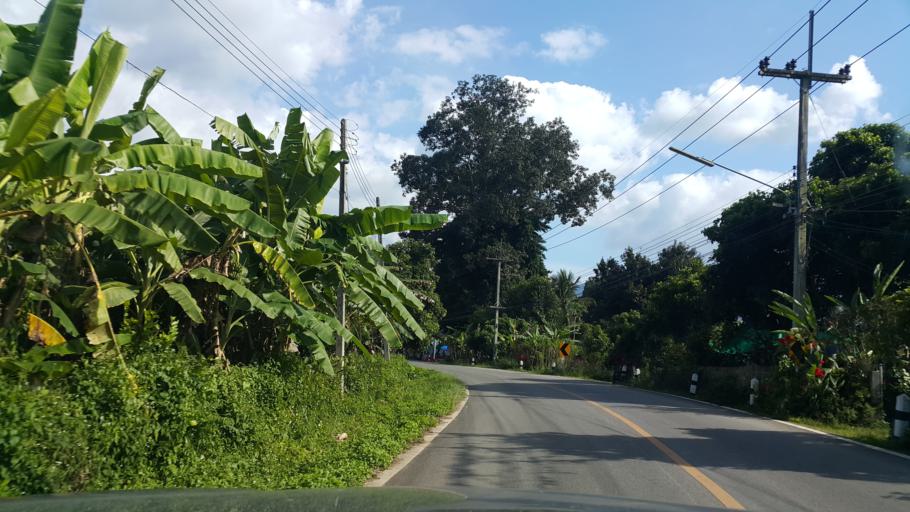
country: TH
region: Lamphun
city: Mae Tha
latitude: 18.5661
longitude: 99.2570
